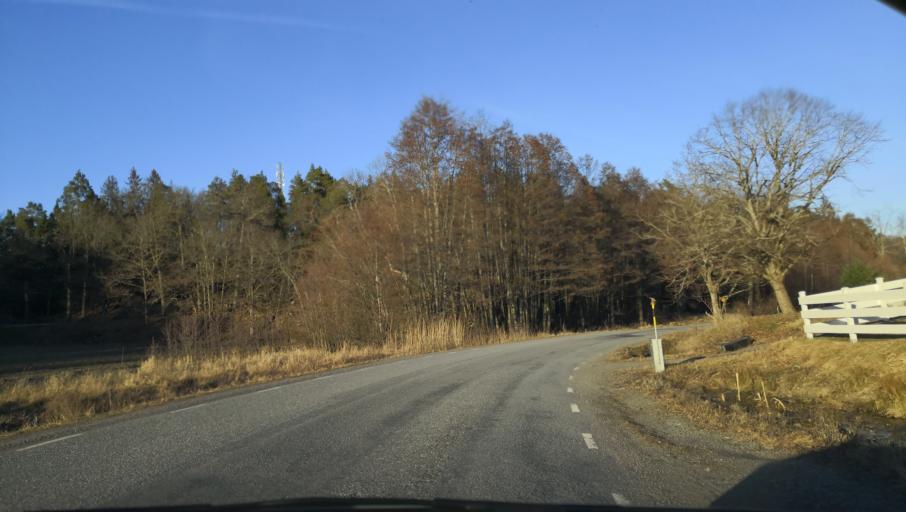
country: SE
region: Stockholm
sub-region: Varmdo Kommun
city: Mortnas
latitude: 59.3325
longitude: 18.4273
